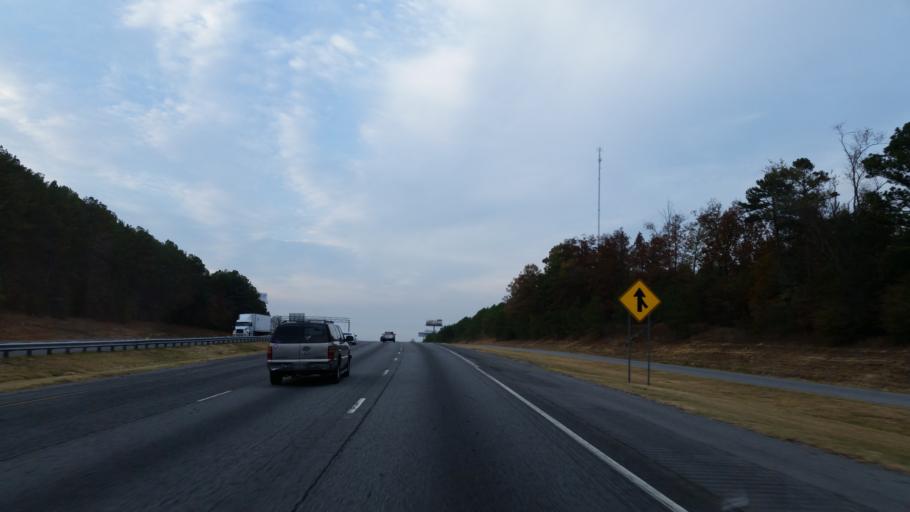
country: US
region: Georgia
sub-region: Gordon County
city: Calhoun
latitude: 34.5438
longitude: -84.9231
